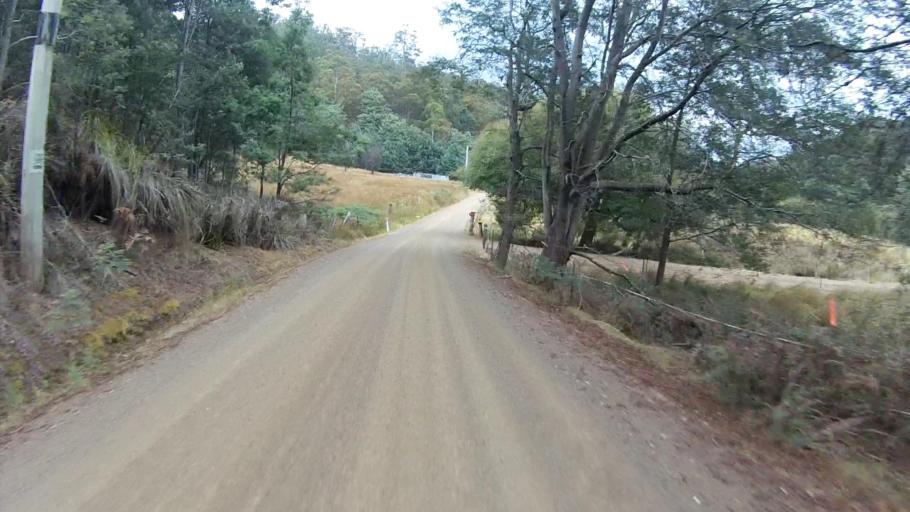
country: AU
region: Tasmania
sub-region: Huon Valley
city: Cygnet
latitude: -43.2250
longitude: 147.1701
